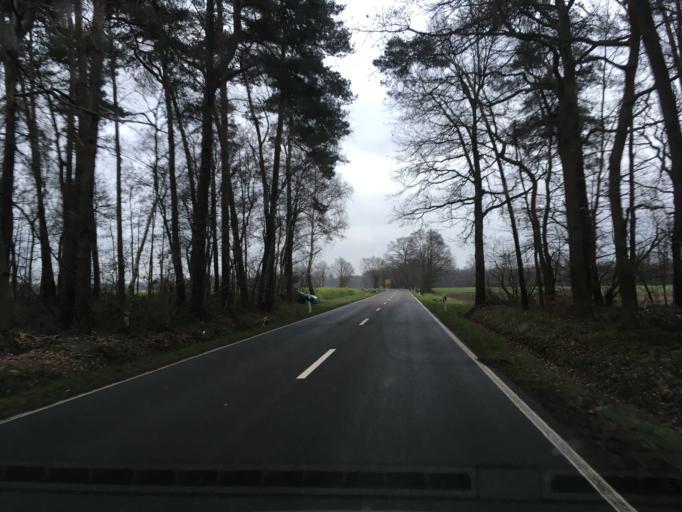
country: DE
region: North Rhine-Westphalia
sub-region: Regierungsbezirk Munster
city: Heek
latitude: 52.1626
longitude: 7.1245
